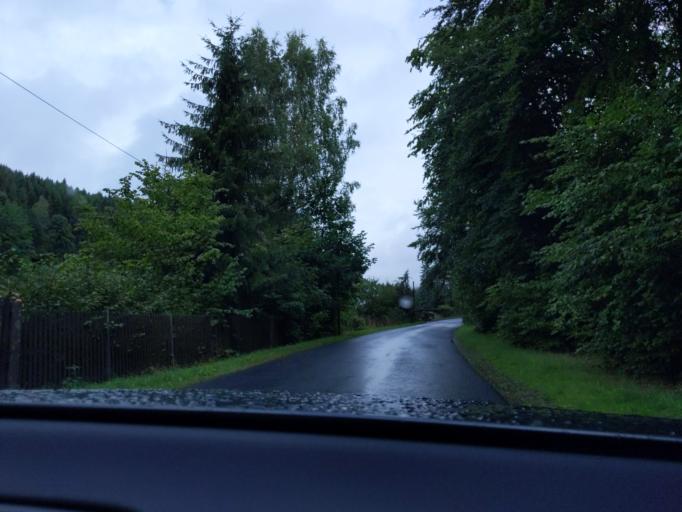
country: DE
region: Thuringia
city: Suhl
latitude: 50.6039
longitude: 10.6570
